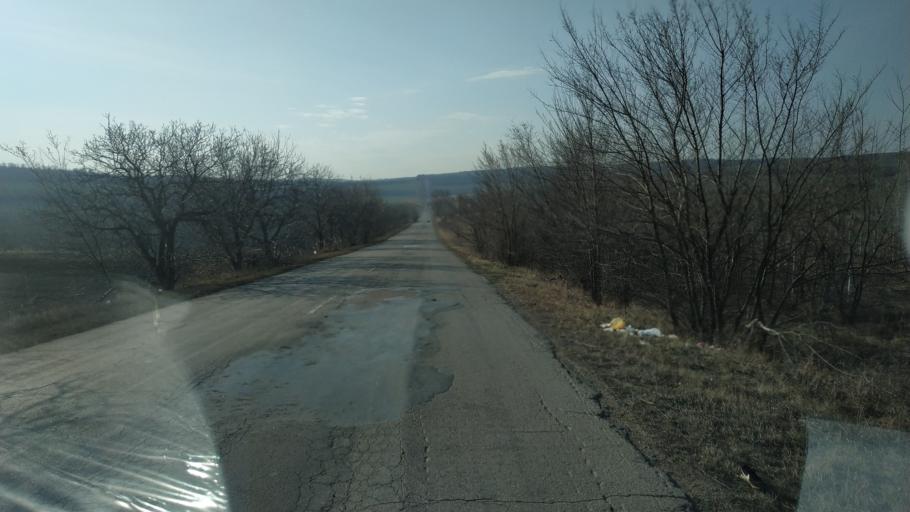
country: MD
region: Chisinau
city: Singera
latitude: 46.8914
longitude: 29.0390
